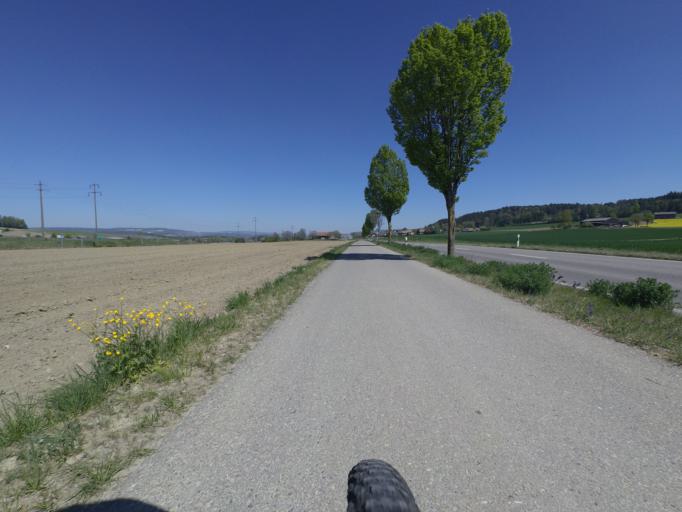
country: CH
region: Zurich
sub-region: Bezirk Winterthur
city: Sulz
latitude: 47.5384
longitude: 8.8114
